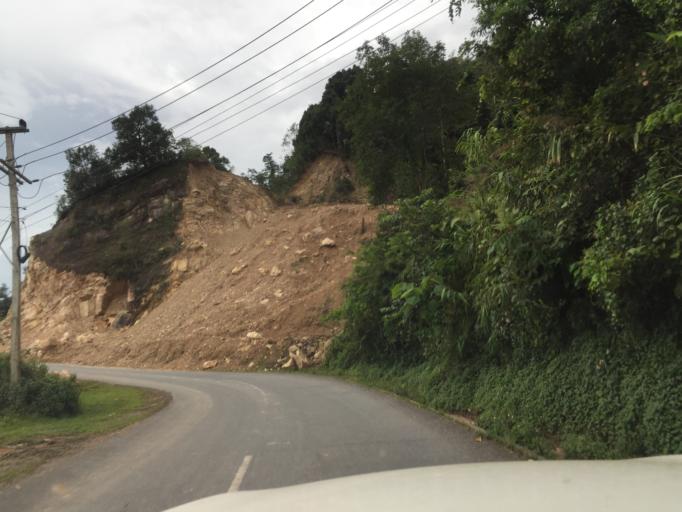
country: LA
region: Phongsali
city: Phongsali
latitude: 21.3124
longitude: 102.0485
